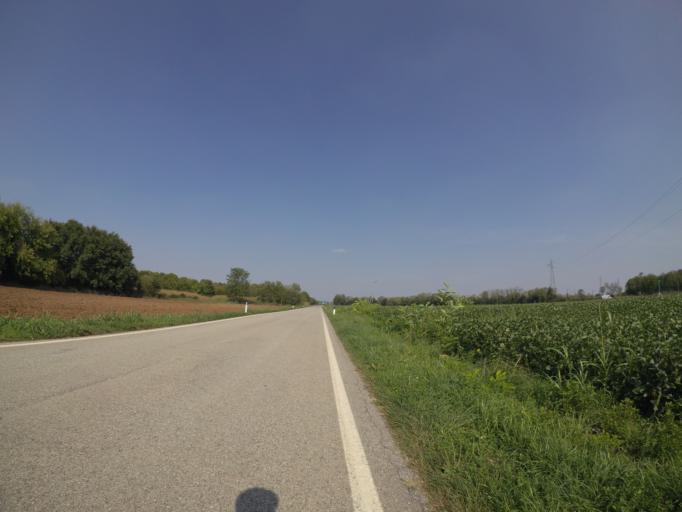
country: IT
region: Friuli Venezia Giulia
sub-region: Provincia di Udine
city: Codroipo
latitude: 45.9802
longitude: 12.9900
